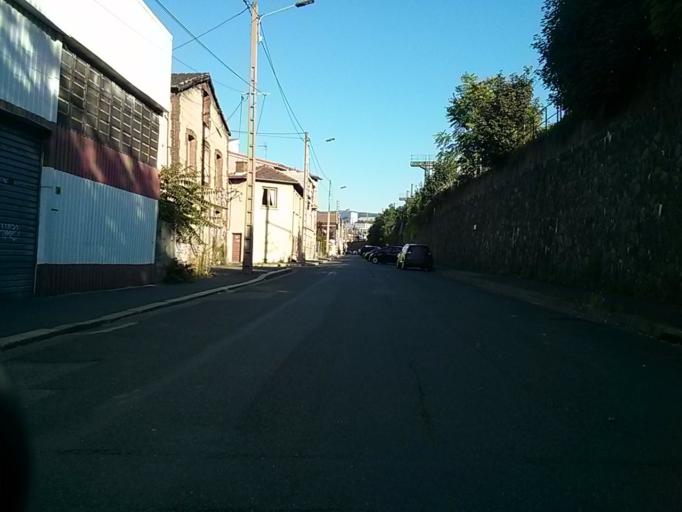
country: FR
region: Rhone-Alpes
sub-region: Departement de la Loire
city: Saint-Etienne
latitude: 45.4464
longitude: 4.3943
